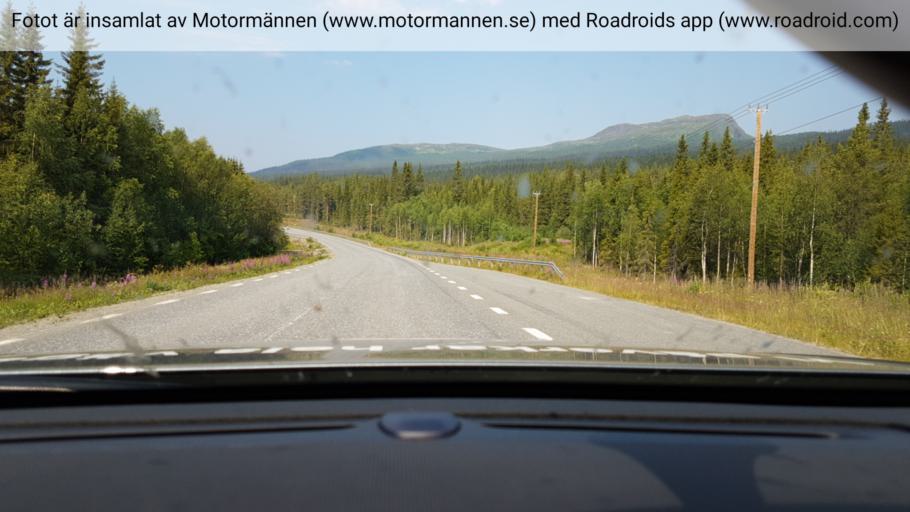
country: SE
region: Vaesterbotten
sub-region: Vilhelmina Kommun
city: Sjoberg
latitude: 65.5041
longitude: 15.7555
